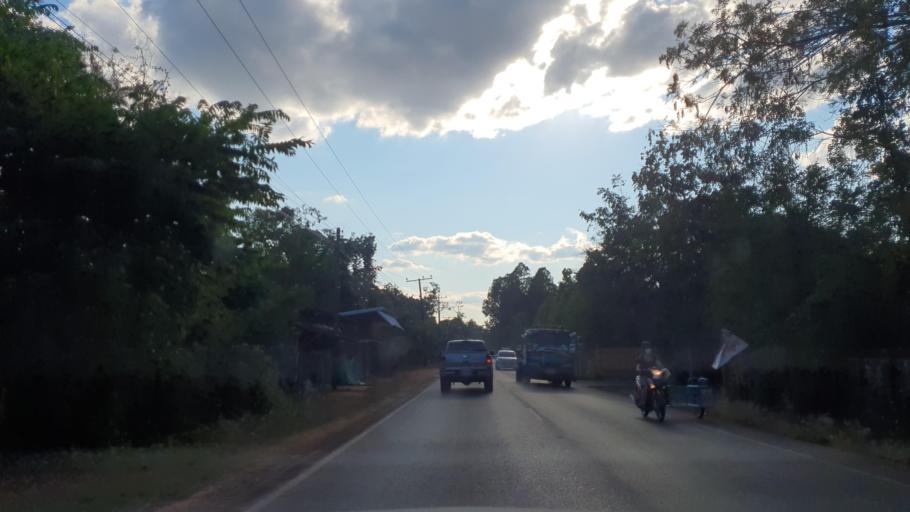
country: TH
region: Changwat Bueng Kan
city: Si Wilai
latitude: 18.1300
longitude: 103.8833
